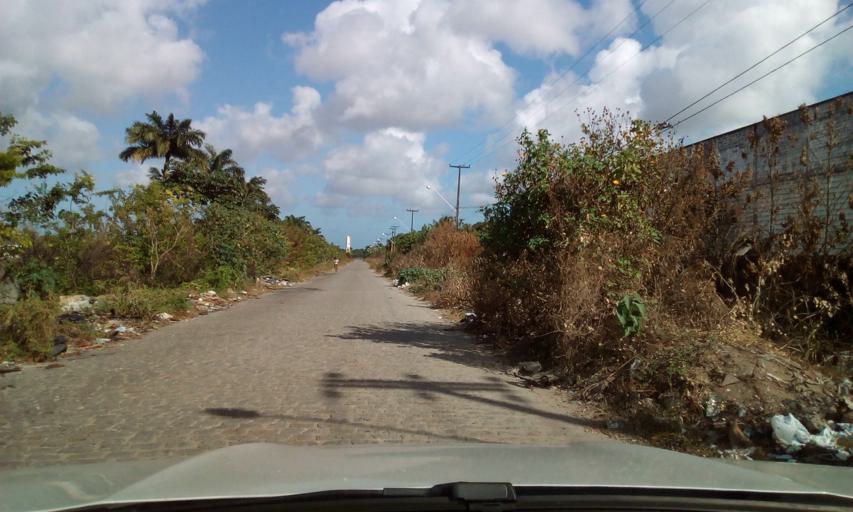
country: BR
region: Paraiba
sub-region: Bayeux
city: Bayeux
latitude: -7.1813
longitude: -34.9152
